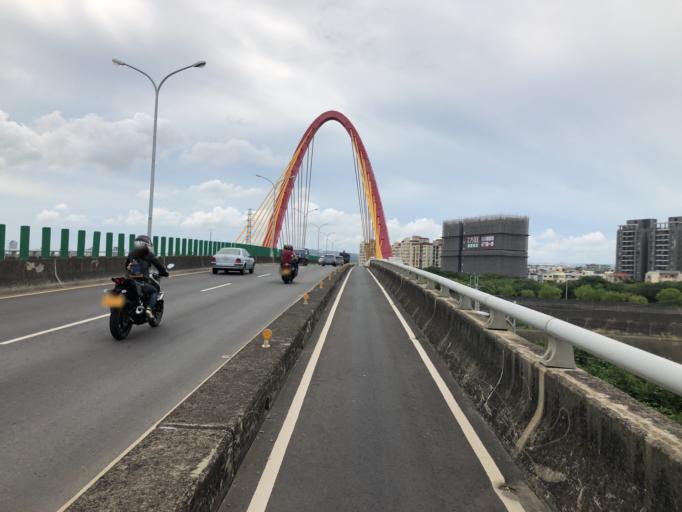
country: TW
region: Taiwan
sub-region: Changhua
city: Chang-hua
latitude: 24.0978
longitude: 120.6266
